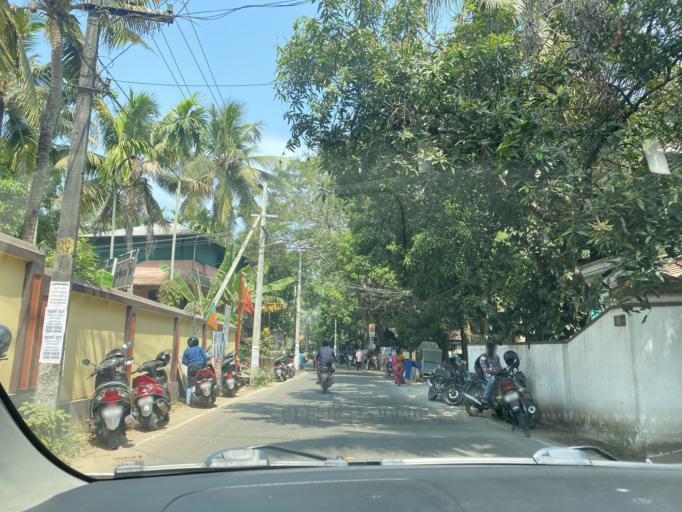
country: IN
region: Kerala
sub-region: Alappuzha
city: Arukutti
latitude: 9.9046
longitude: 76.3210
